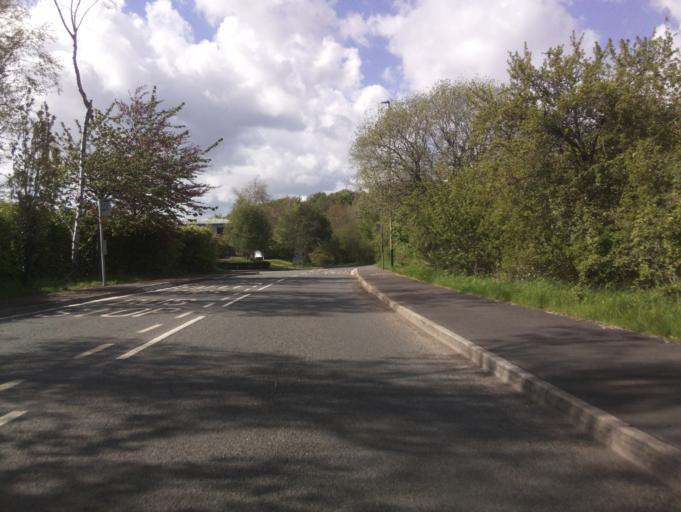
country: GB
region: Wales
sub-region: Caerphilly County Borough
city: Caerphilly
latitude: 51.5710
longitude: -3.2001
